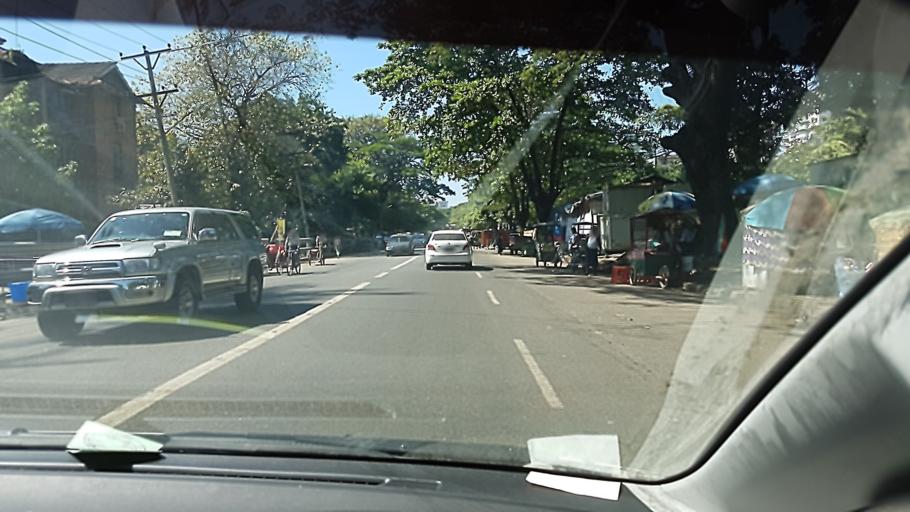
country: MM
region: Yangon
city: Yangon
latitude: 16.7836
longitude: 96.1662
